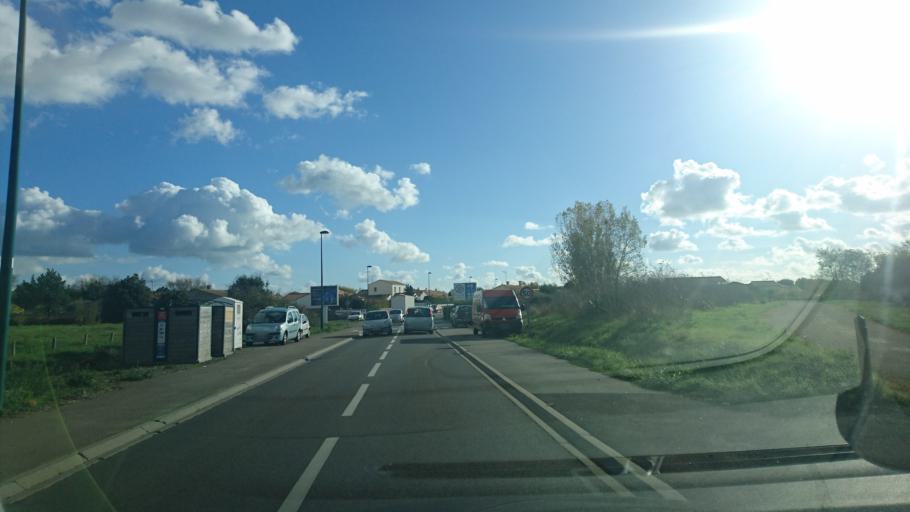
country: FR
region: Pays de la Loire
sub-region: Departement de la Vendee
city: Les Sables-d'Olonne
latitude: 46.5176
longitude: -1.7910
